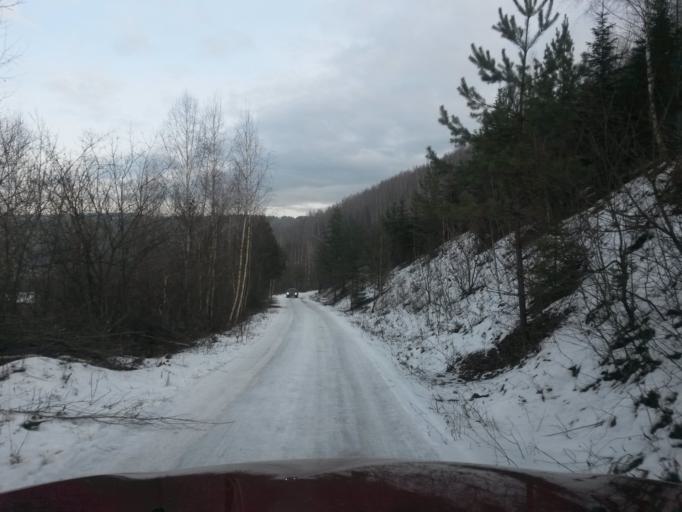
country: SK
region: Kosicky
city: Spisska Nova Ves
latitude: 48.8987
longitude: 20.6504
